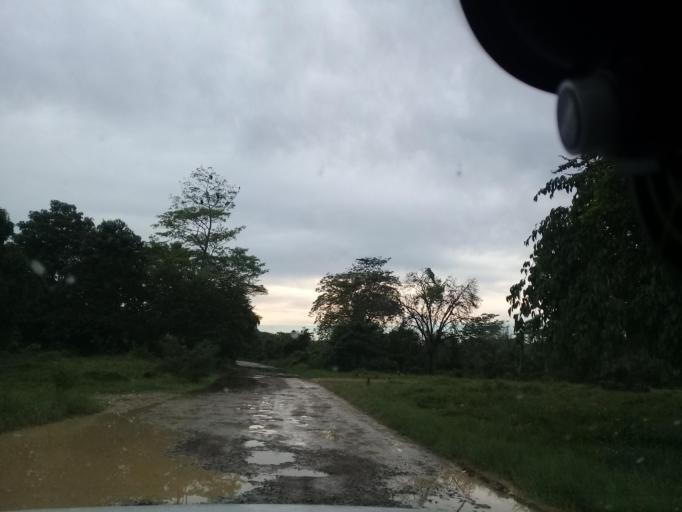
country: MX
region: Hidalgo
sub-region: Huejutla de Reyes
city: Chalahuiyapa
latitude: 21.1582
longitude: -98.3696
